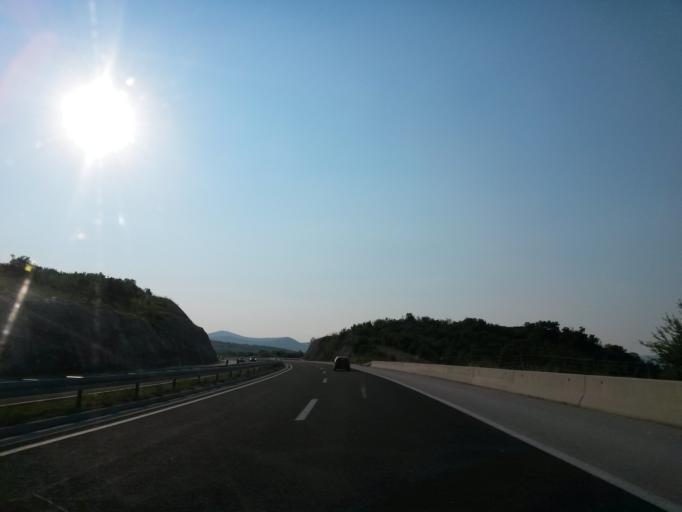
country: HR
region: Splitsko-Dalmatinska
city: Dugopolje
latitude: 43.5858
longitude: 16.6411
